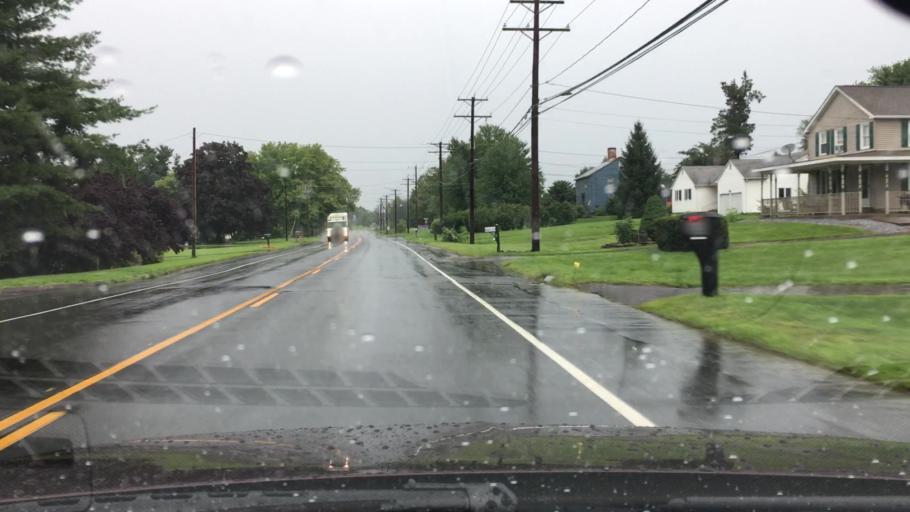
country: US
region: Connecticut
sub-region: Hartford County
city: Windsor Locks
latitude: 41.9445
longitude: -72.6026
